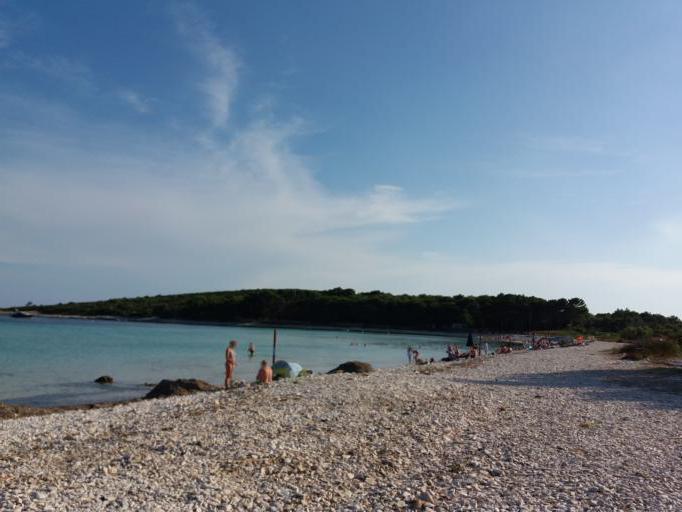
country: HR
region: Zadarska
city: Ugljan
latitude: 44.1345
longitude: 14.8728
